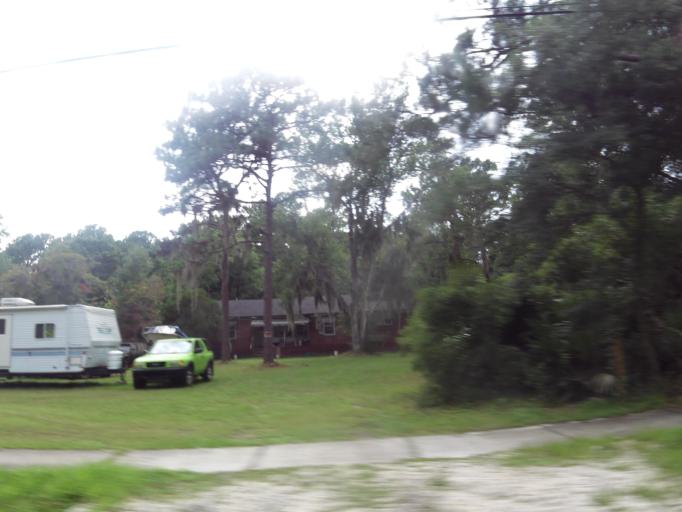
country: US
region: Florida
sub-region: Duval County
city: Jacksonville
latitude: 30.2964
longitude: -81.5297
